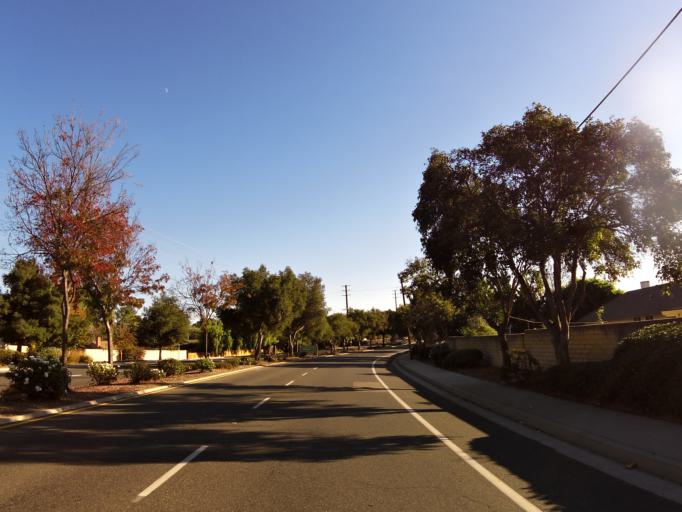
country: US
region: California
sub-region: Ventura County
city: Moorpark
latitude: 34.2265
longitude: -118.8689
